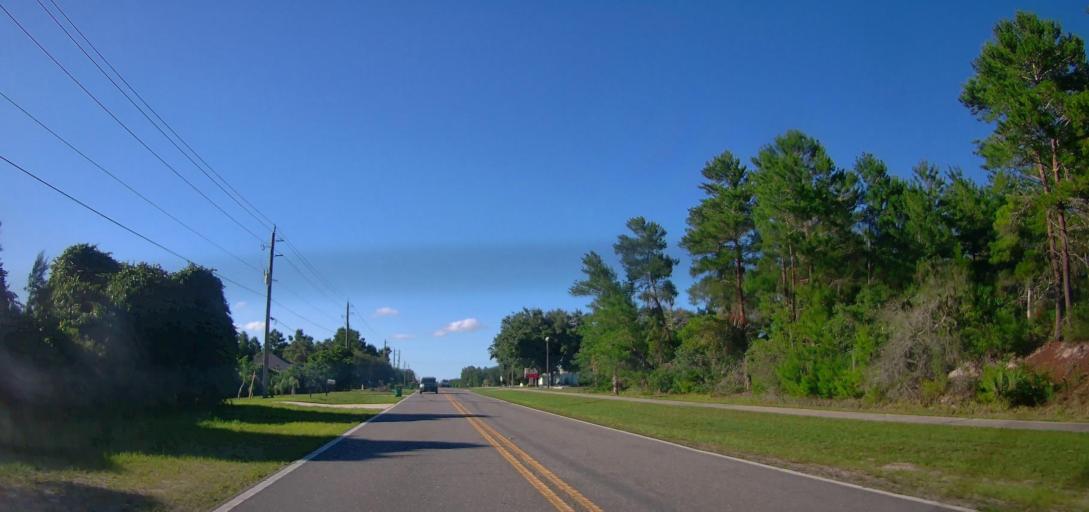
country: US
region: Florida
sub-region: Brevard County
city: Titusville
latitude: 28.5453
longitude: -80.8227
